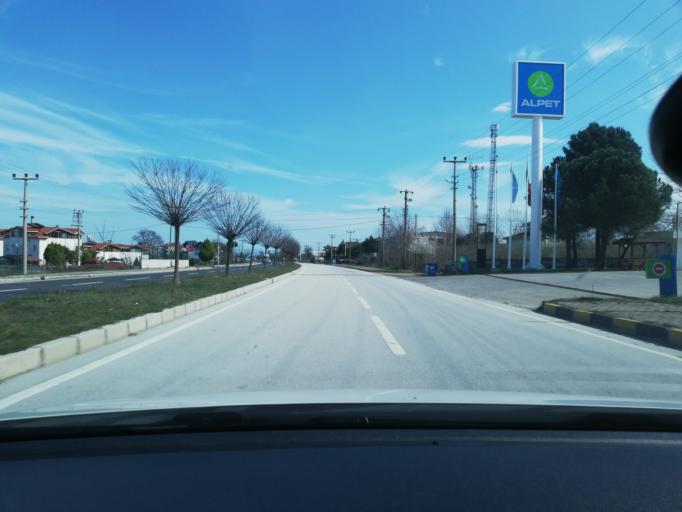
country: TR
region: Duzce
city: Akcakoca
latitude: 41.0881
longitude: 31.1820
